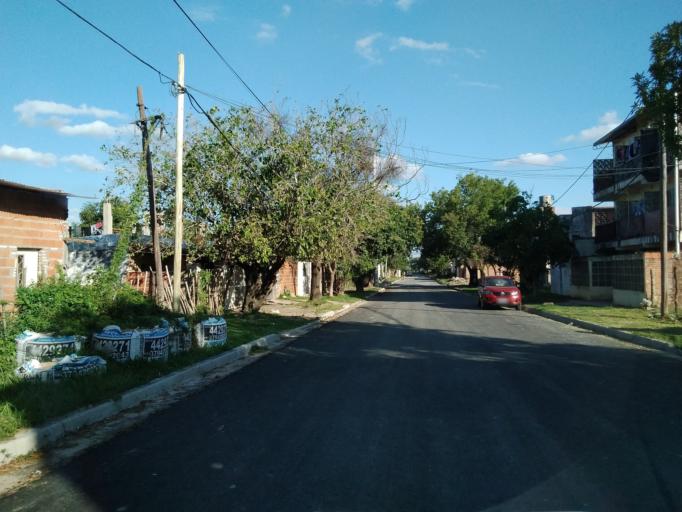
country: AR
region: Corrientes
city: Corrientes
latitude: -27.4622
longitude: -58.7812
